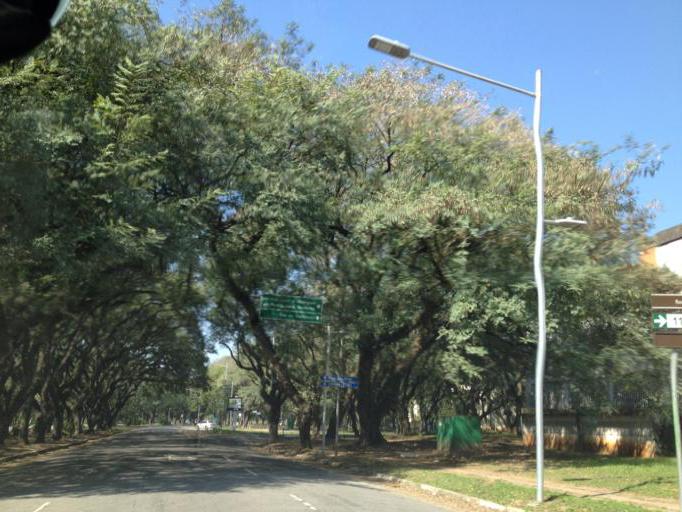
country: BR
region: Sao Paulo
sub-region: Osasco
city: Osasco
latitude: -23.5541
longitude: -46.7260
